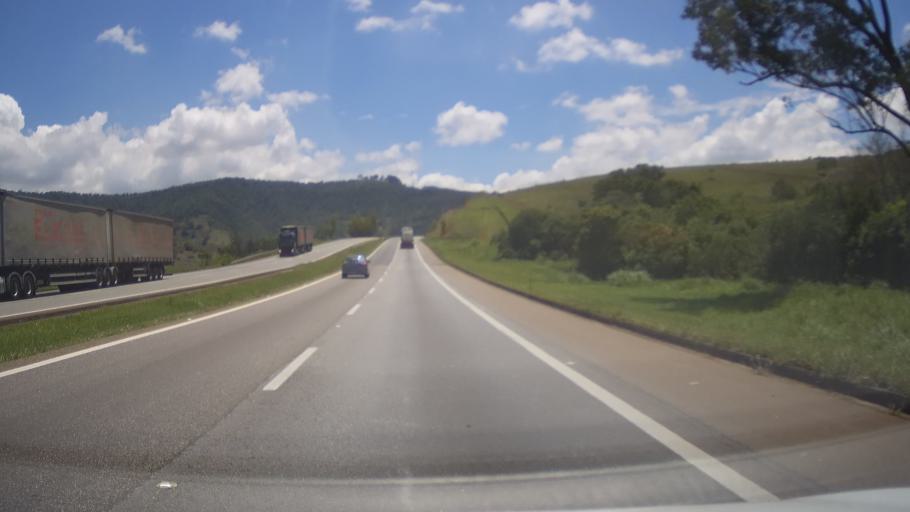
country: BR
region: Minas Gerais
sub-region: Campanha
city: Campanha
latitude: -21.8194
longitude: -45.4932
